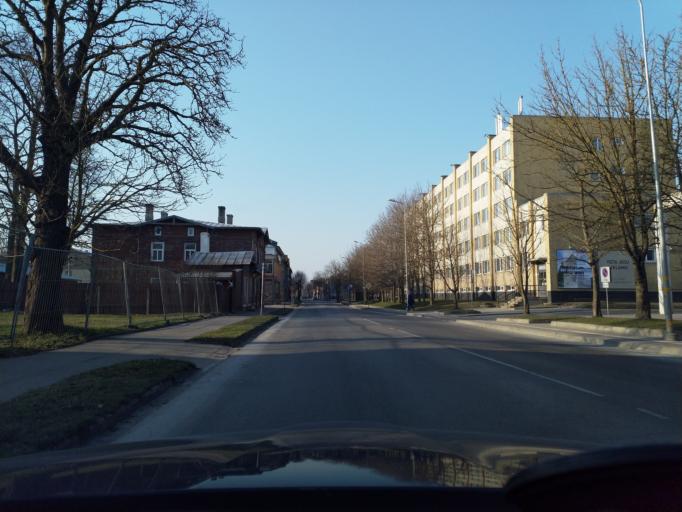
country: LV
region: Liepaja
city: Liepaja
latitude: 56.5060
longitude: 21.0202
